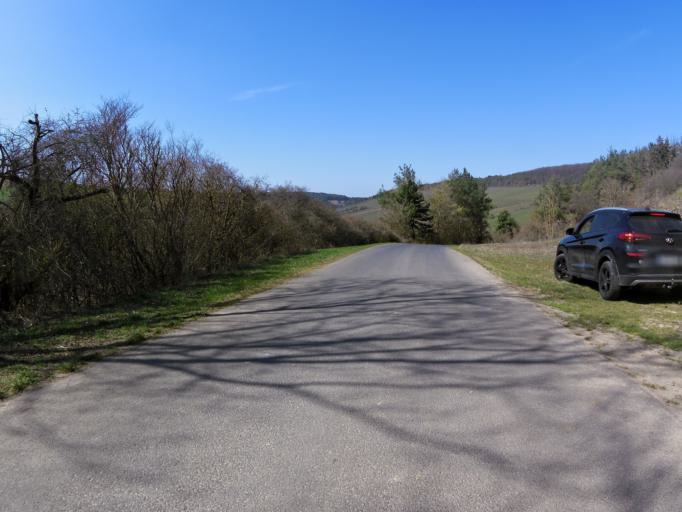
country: DE
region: Bavaria
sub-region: Regierungsbezirk Unterfranken
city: Erlabrunn
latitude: 49.8419
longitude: 9.8233
